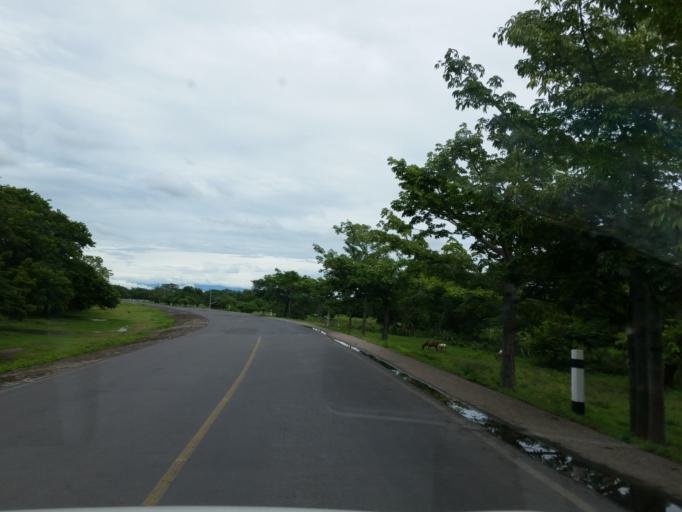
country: NI
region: Chinandega
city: Somotillo
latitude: 12.8077
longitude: -86.9028
